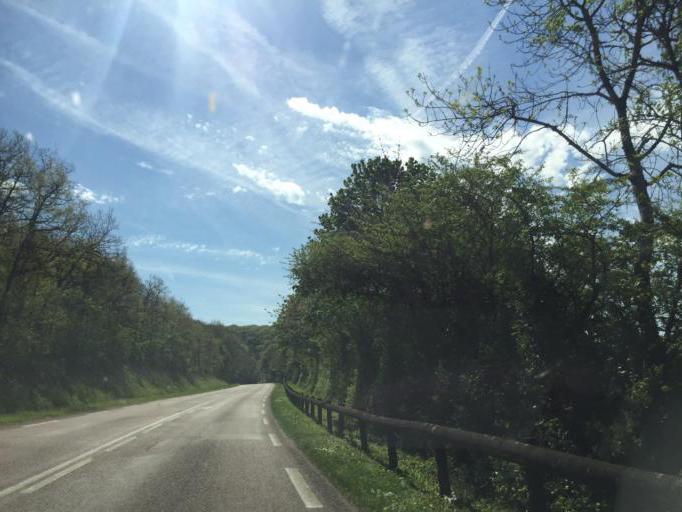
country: FR
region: Bourgogne
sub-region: Departement de la Nievre
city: Clamecy
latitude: 47.4486
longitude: 3.5541
